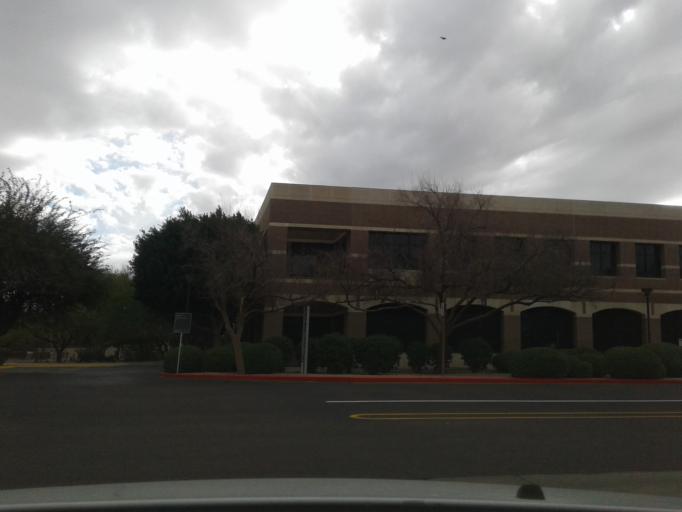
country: US
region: Arizona
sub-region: Maricopa County
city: Glendale
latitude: 33.6095
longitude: -112.1587
